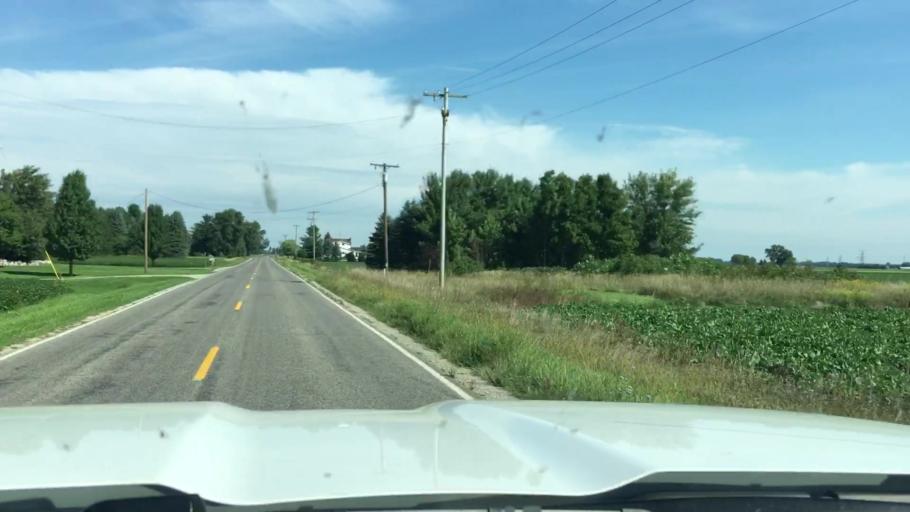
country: US
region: Michigan
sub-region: Saginaw County
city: Hemlock
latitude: 43.4978
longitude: -84.2297
